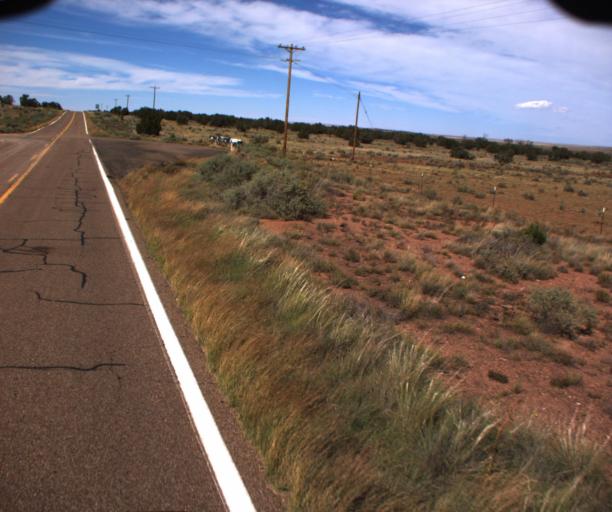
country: US
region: Arizona
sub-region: Apache County
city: Saint Johns
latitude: 34.6111
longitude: -109.6582
